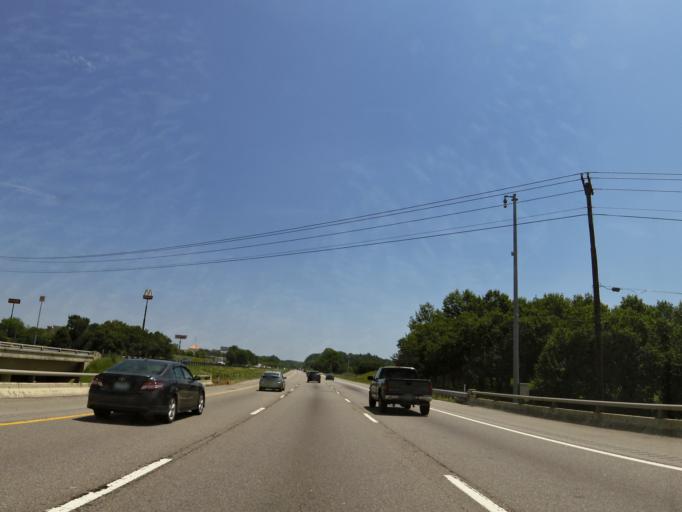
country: US
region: Tennessee
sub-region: Knox County
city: Mascot
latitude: 36.0027
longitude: -83.7754
